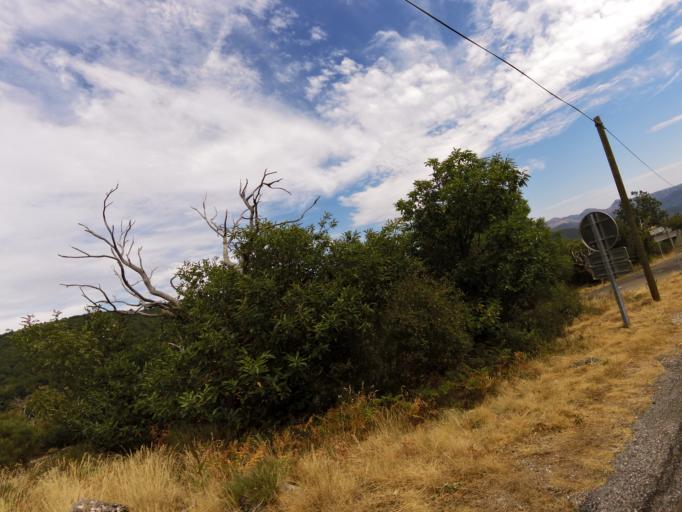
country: FR
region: Languedoc-Roussillon
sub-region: Departement du Gard
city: Valleraugue
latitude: 44.0350
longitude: 3.6205
